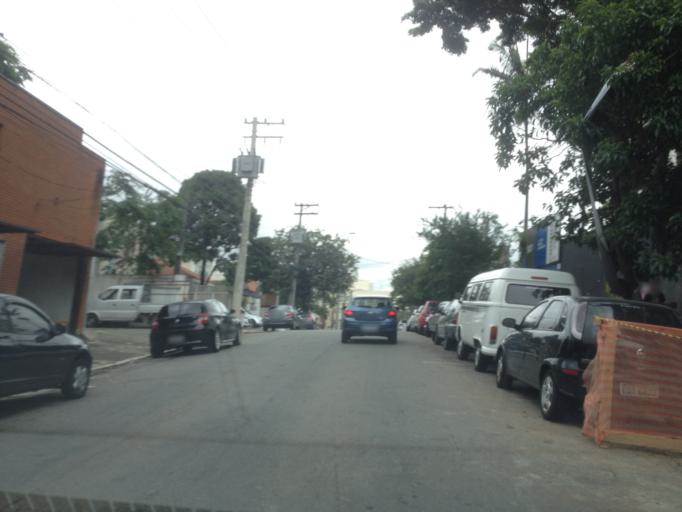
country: BR
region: Sao Paulo
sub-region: Sao Paulo
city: Sao Paulo
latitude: -23.5563
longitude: -46.6926
